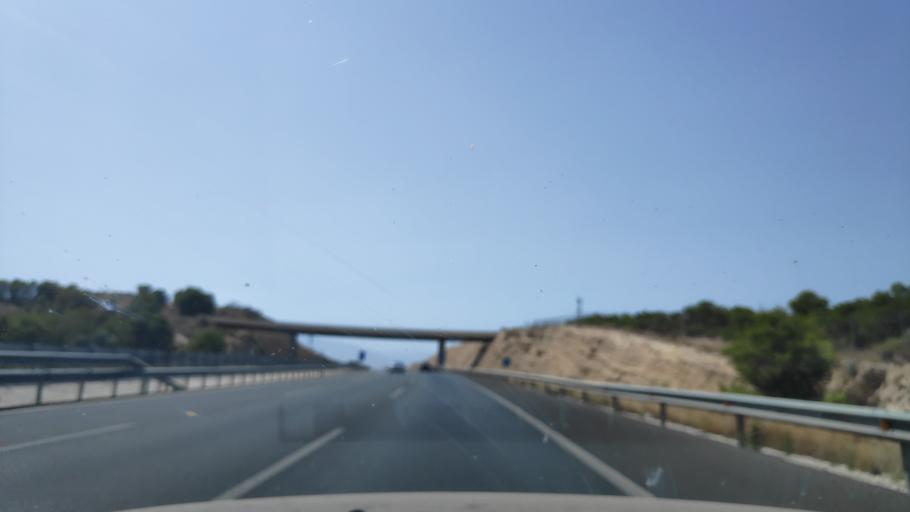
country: ES
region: Murcia
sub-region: Murcia
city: Molina de Segura
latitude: 38.0456
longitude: -1.1665
